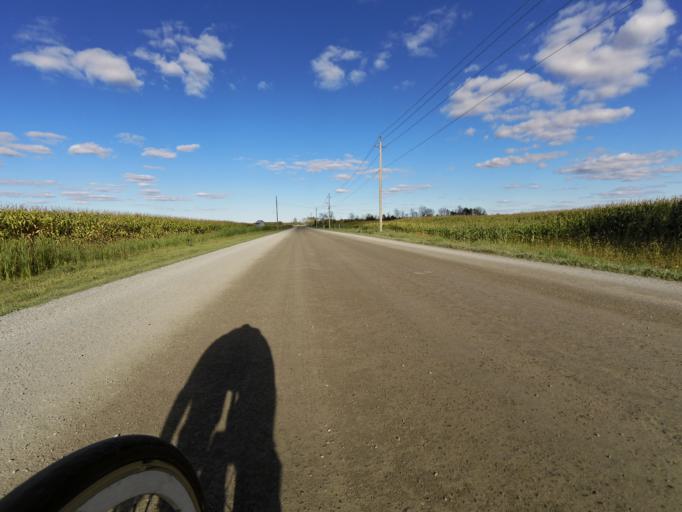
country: CA
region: Ontario
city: Bells Corners
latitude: 45.1136
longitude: -75.7093
